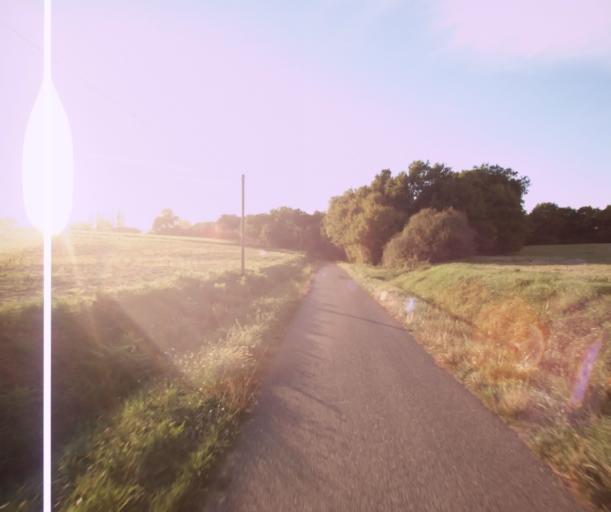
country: FR
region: Midi-Pyrenees
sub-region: Departement du Gers
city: Eauze
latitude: 43.8899
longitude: 0.0655
